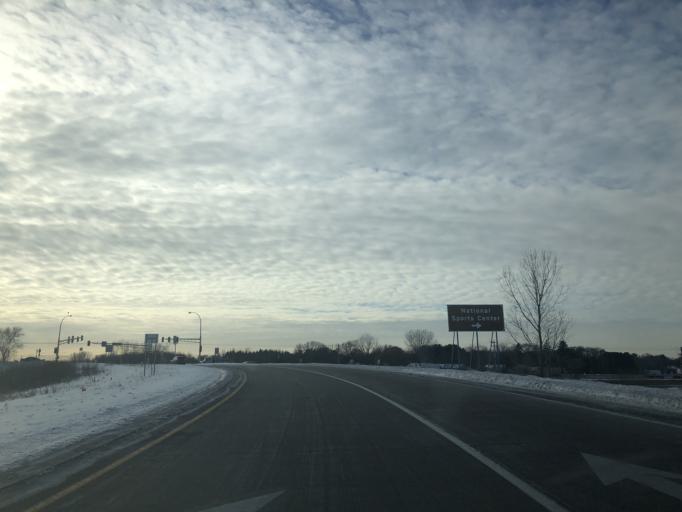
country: US
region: Minnesota
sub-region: Anoka County
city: Lexington
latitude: 45.1437
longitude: -93.1860
